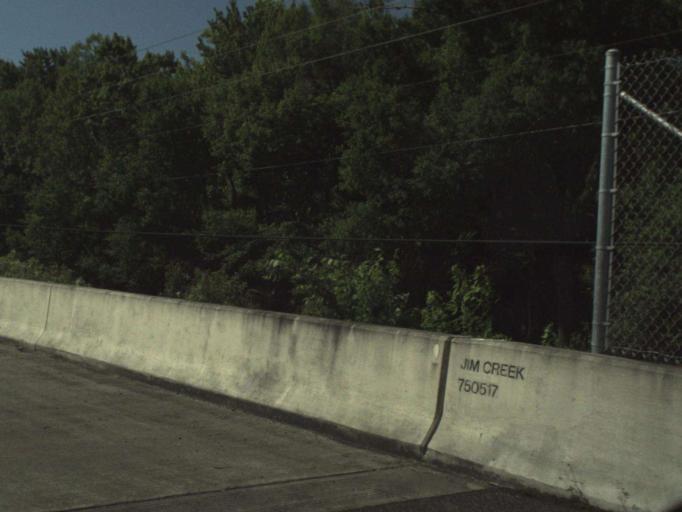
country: US
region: Florida
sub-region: Orange County
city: Christmas
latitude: 28.4359
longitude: -80.9664
